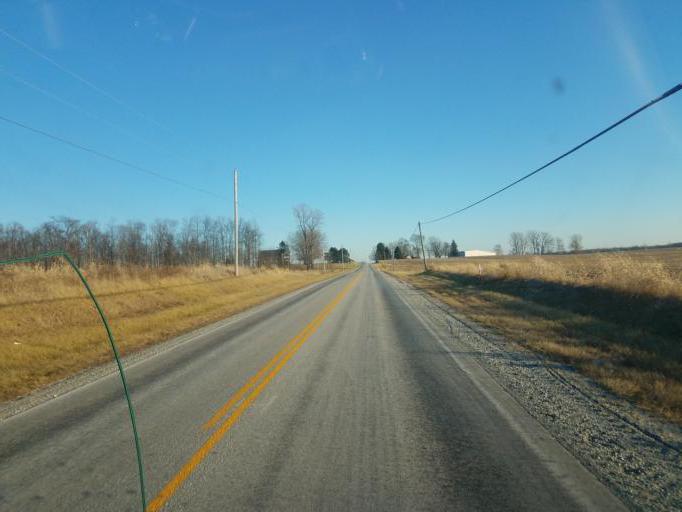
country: US
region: Ohio
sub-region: Hardin County
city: Kenton
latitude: 40.6358
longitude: -83.5548
